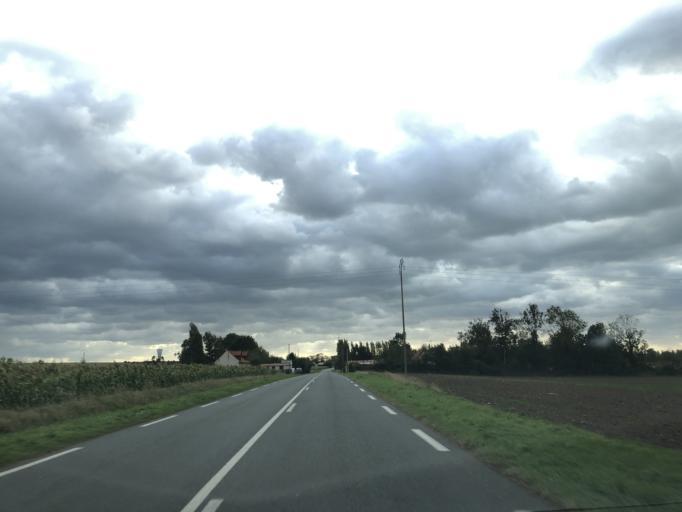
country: FR
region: Picardie
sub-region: Departement de la Somme
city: Pende
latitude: 50.1449
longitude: 1.5345
